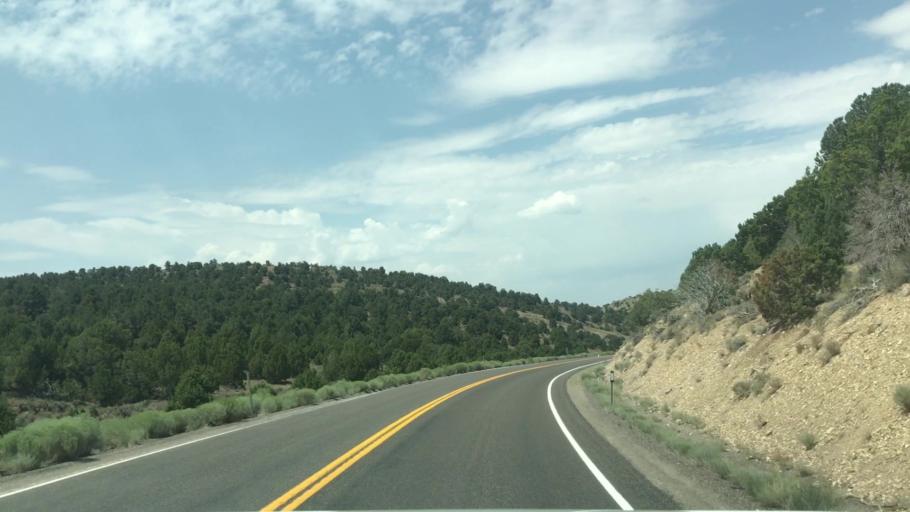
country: US
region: Nevada
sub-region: Eureka County
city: Eureka
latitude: 39.3956
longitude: -115.4780
